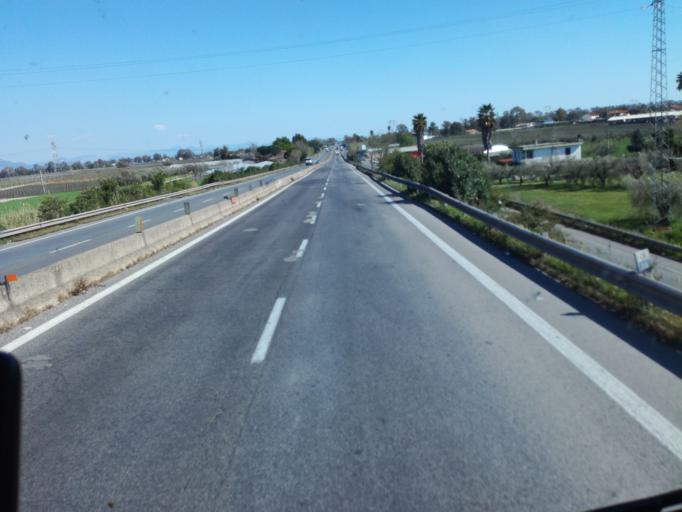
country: IT
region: Latium
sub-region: Provincia di Latina
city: Borgo Podgora
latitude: 41.5148
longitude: 12.7849
